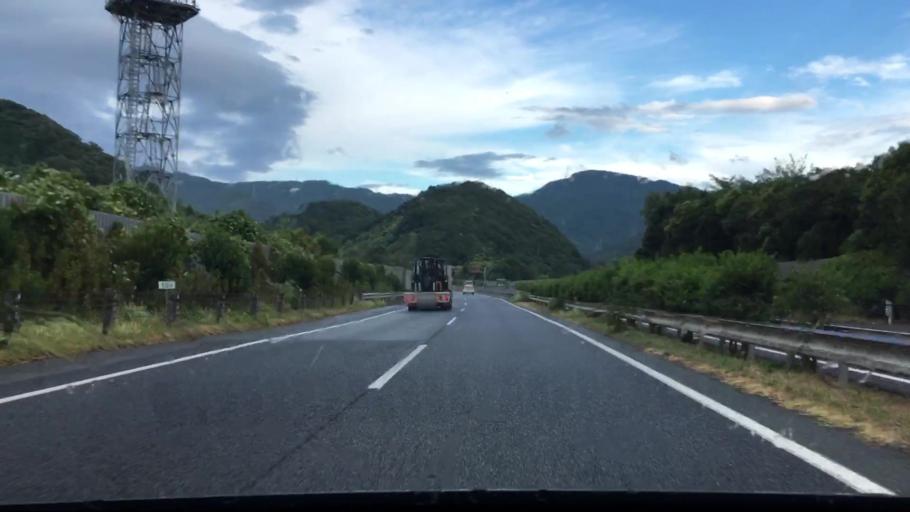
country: JP
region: Fukuoka
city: Kitakyushu
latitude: 33.8020
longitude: 130.8578
